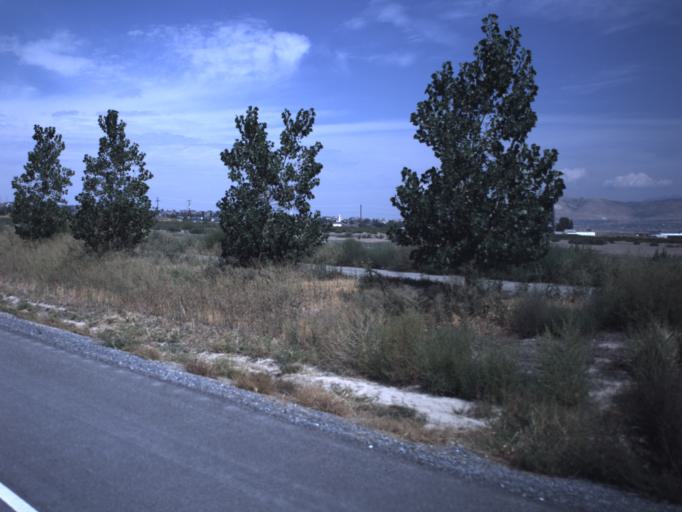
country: US
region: Utah
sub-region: Utah County
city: Saratoga Springs
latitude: 40.3804
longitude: -111.9270
